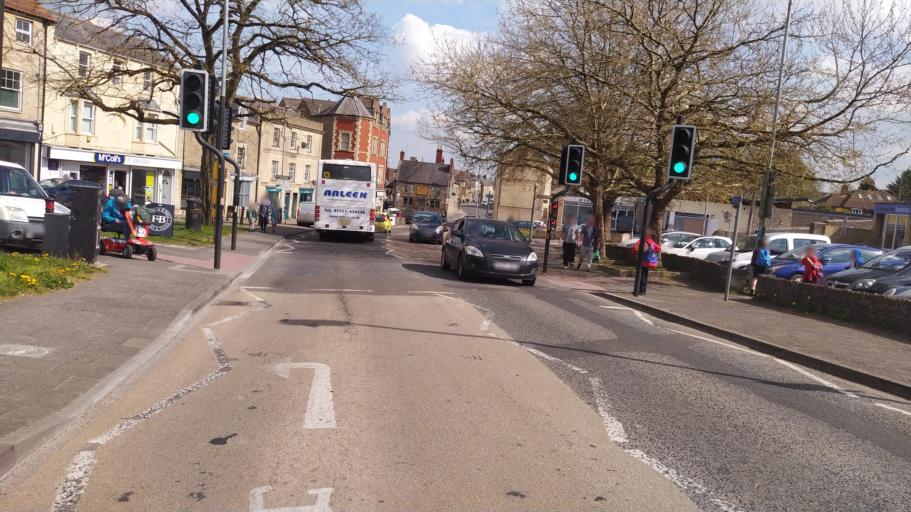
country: GB
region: England
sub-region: Somerset
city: Frome
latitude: 51.2310
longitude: -2.3286
